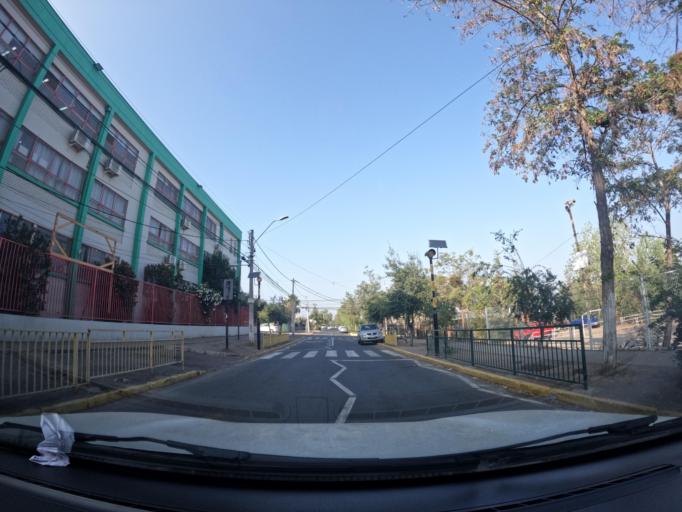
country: CL
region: Santiago Metropolitan
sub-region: Provincia de Santiago
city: Villa Presidente Frei, Nunoa, Santiago, Chile
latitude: -33.4661
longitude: -70.5350
